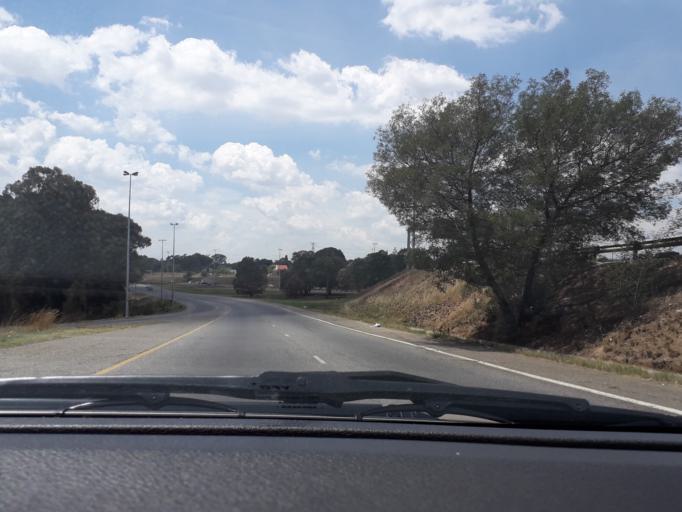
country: ZA
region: Gauteng
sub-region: City of Johannesburg Metropolitan Municipality
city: Johannesburg
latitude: -26.2567
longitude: 27.9868
